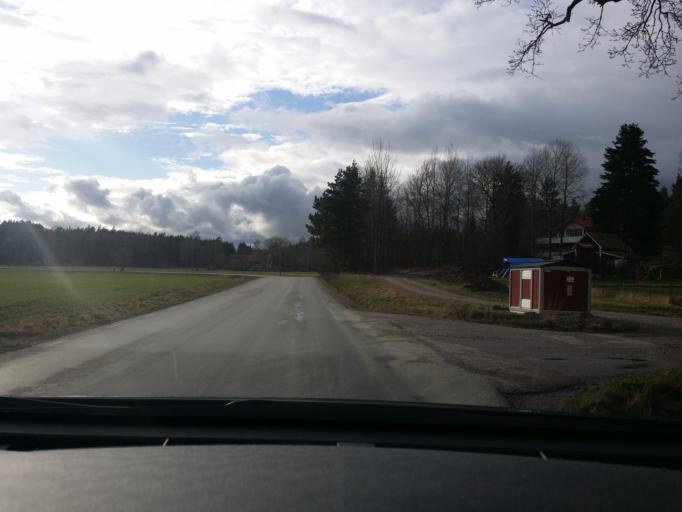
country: SE
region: Soedermanland
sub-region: Eskilstuna Kommun
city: Arla
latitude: 59.3270
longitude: 16.6686
